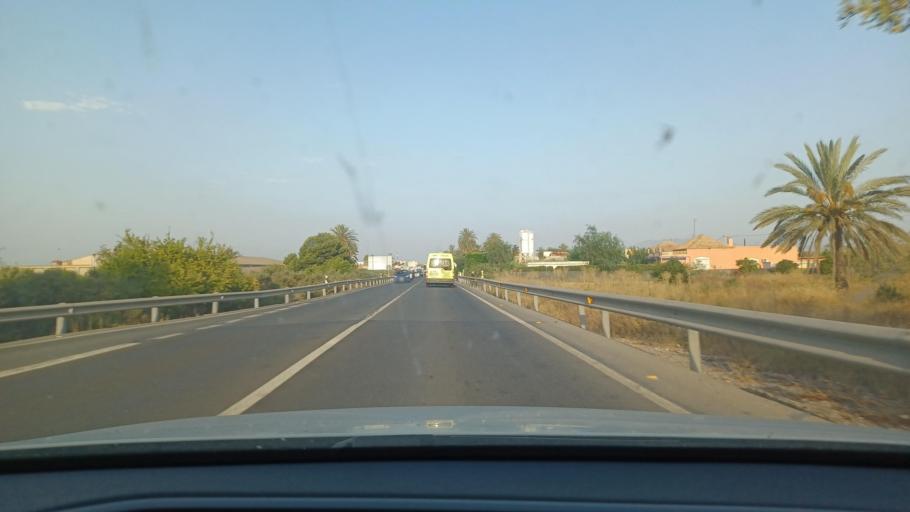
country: ES
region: Valencia
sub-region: Provincia de Alicante
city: Elche
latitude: 38.2770
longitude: -0.6532
